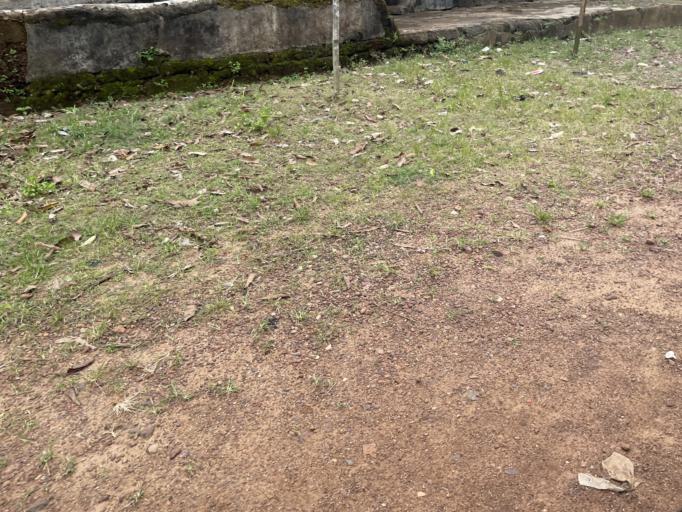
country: SL
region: Northern Province
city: Kambia
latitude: 9.1297
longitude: -12.9077
